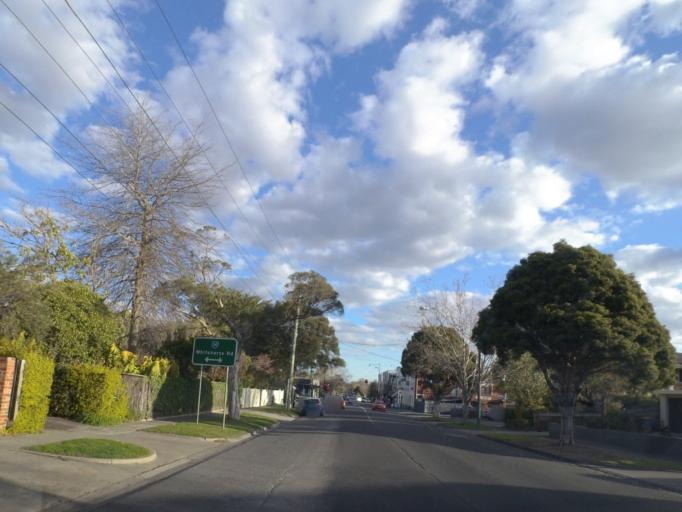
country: AU
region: Victoria
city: Mont Albert
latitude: -37.8140
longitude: 145.0996
